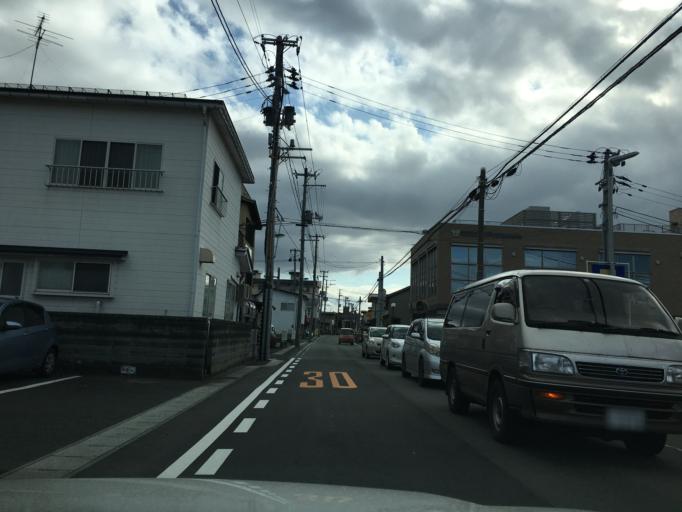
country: JP
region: Yamagata
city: Yamagata-shi
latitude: 38.2598
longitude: 140.3254
